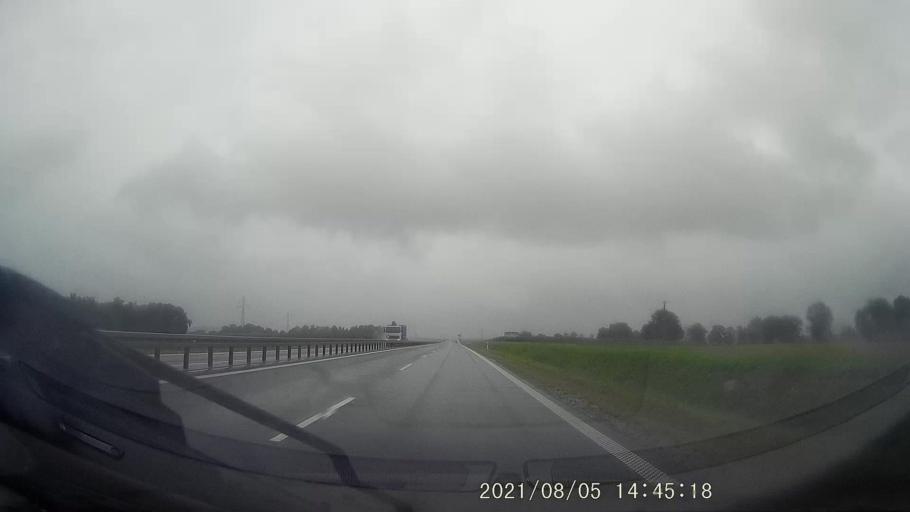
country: PL
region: Opole Voivodeship
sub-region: Powiat nyski
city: Nysa
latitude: 50.4987
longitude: 17.3622
